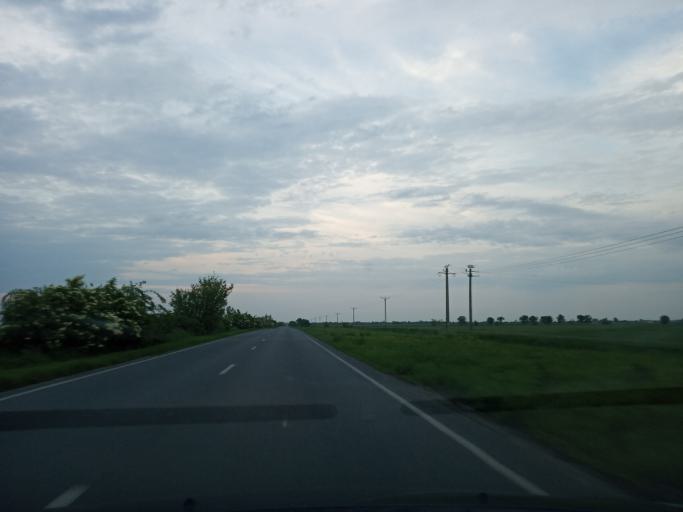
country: RO
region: Timis
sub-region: Comuna Voiteg
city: Voiteg
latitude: 45.4454
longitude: 21.2329
